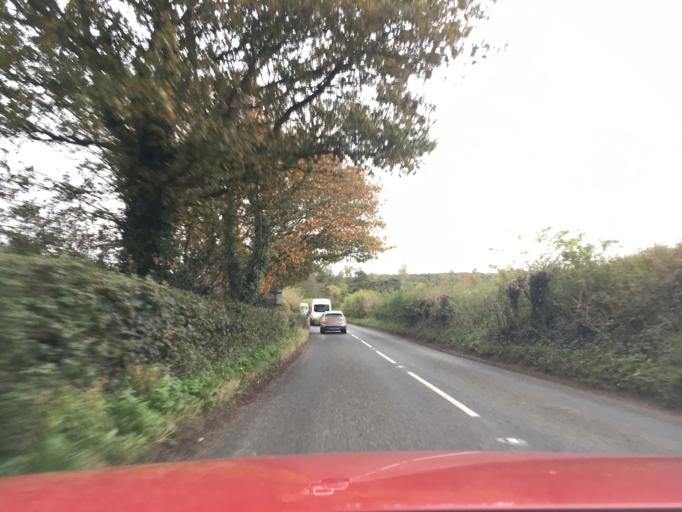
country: GB
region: England
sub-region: Dorset
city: Sherborne
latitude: 50.9709
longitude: -2.5550
